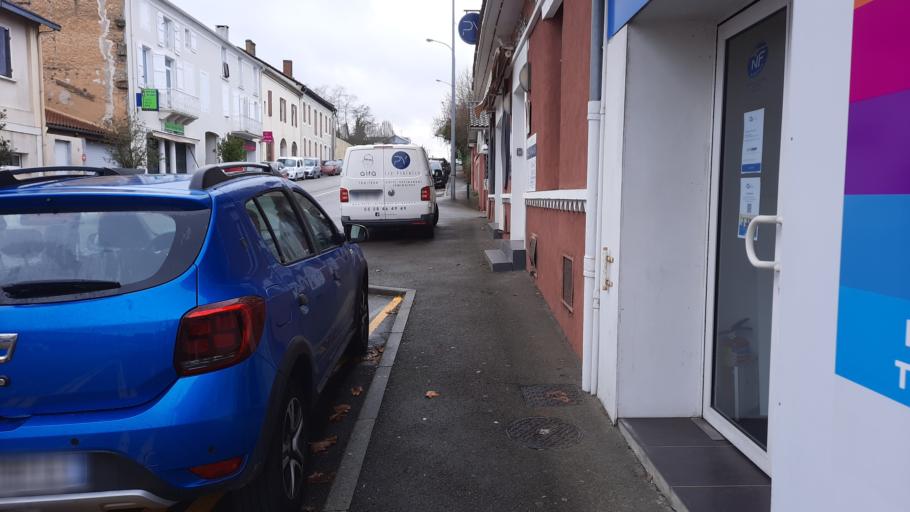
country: FR
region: Aquitaine
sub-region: Departement des Landes
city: Mont-de-Marsan
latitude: 43.8868
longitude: -0.5002
